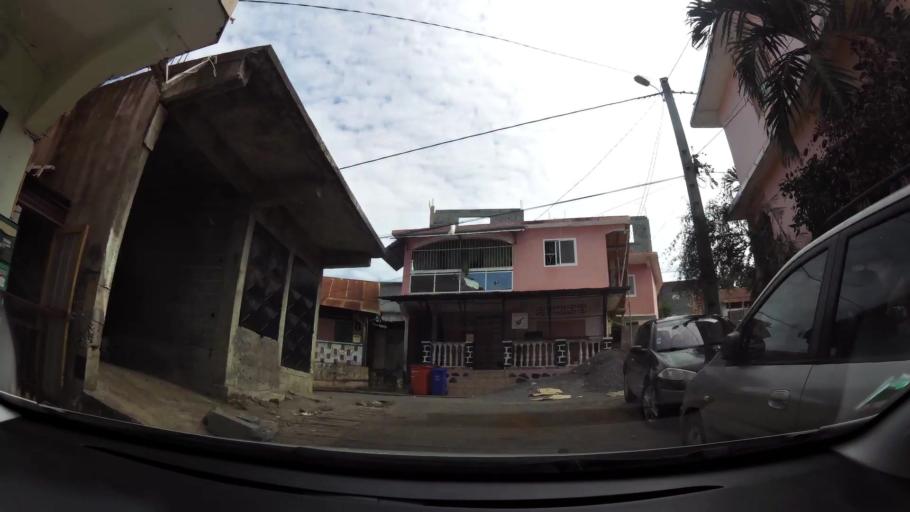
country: YT
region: Mamoudzou
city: Mamoudzou
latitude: -12.7811
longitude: 45.2313
